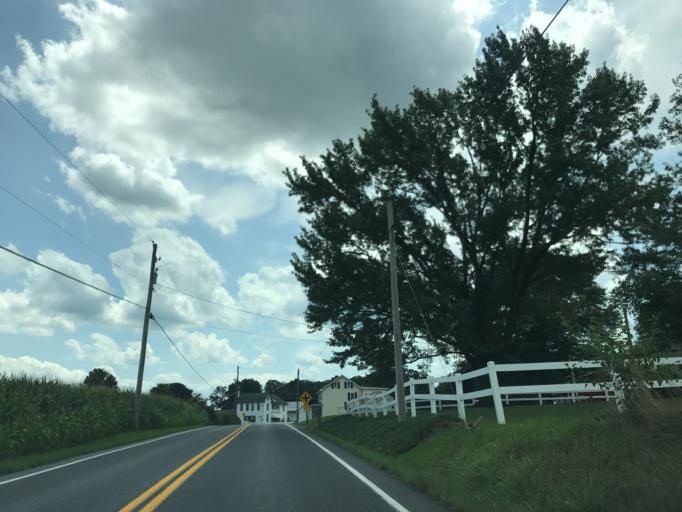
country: US
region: Pennsylvania
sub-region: Lancaster County
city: Manheim
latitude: 40.1922
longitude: -76.4534
